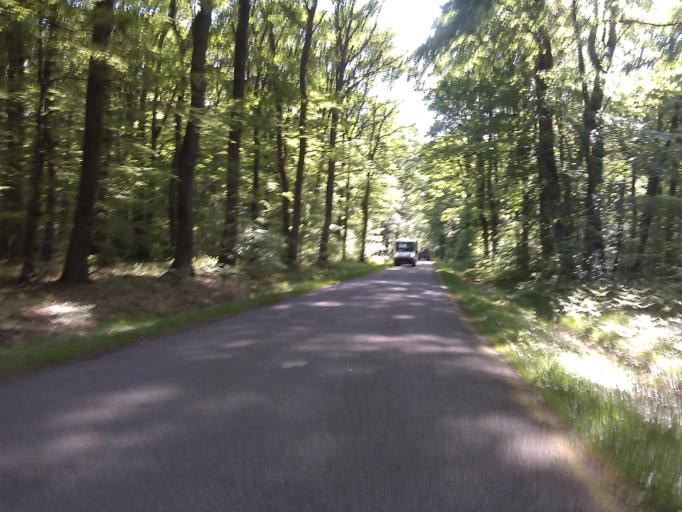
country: FR
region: Auvergne
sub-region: Departement de l'Allier
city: Lurcy-Levis
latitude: 46.6184
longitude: 2.9455
